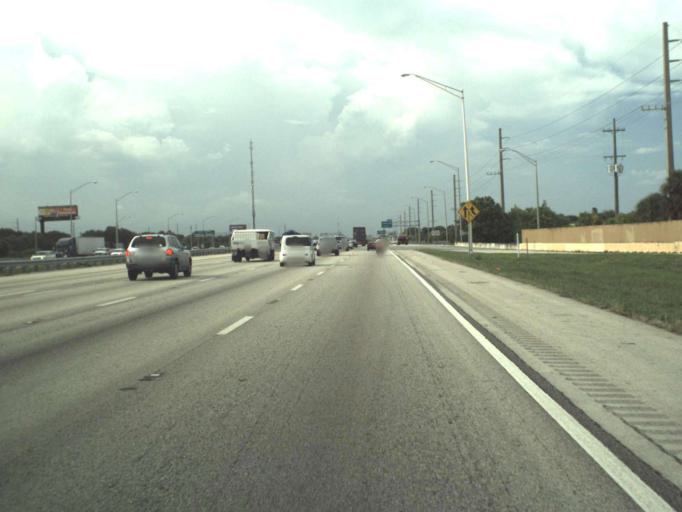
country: US
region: Florida
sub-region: Palm Beach County
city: Highland Beach
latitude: 26.4231
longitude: -80.0898
